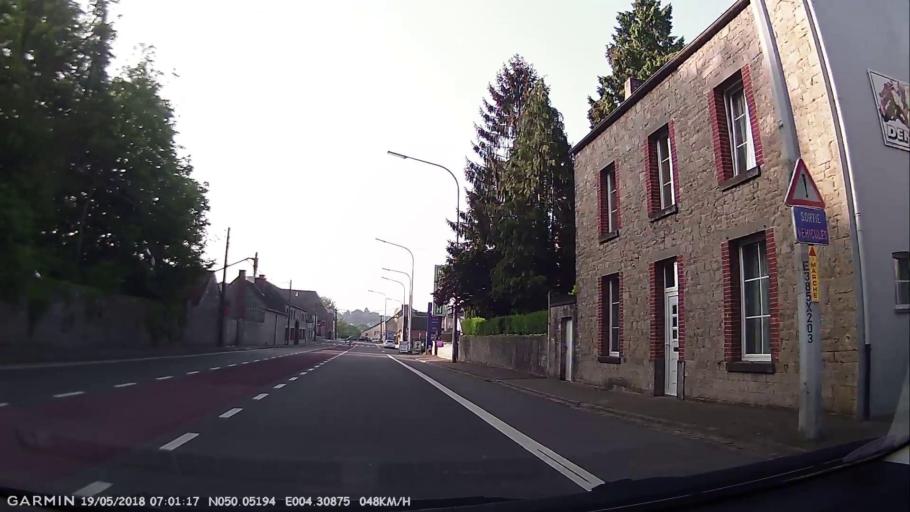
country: BE
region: Wallonia
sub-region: Province du Hainaut
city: Chimay
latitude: 50.0518
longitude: 4.3088
